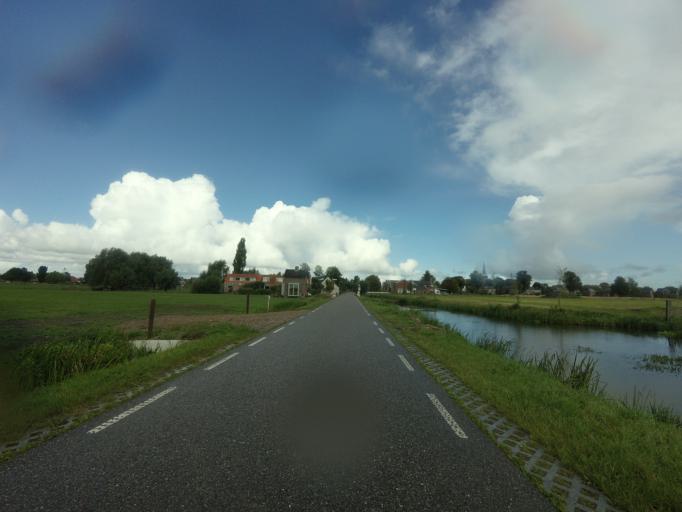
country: NL
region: Friesland
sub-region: Gemeente Leeuwarden
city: Wirdum
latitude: 53.1460
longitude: 5.8028
